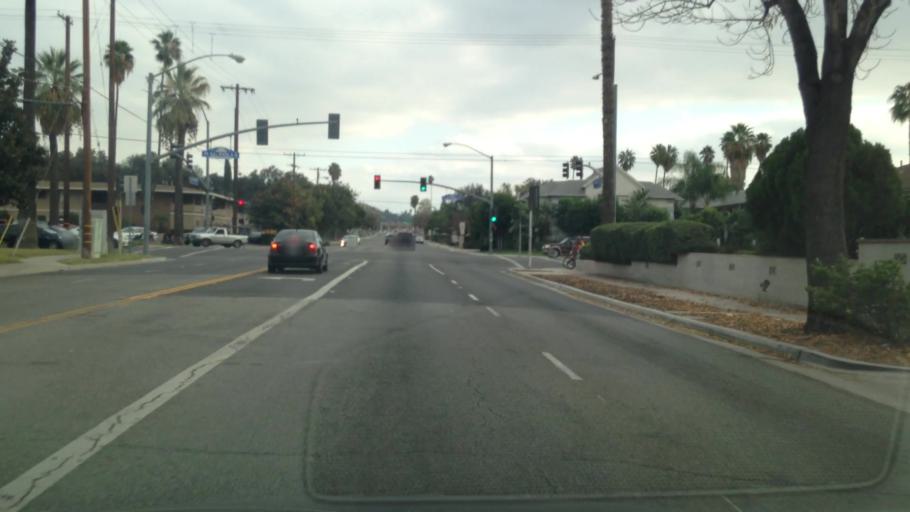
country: US
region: California
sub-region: Riverside County
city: Riverside
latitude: 33.9419
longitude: -117.4099
